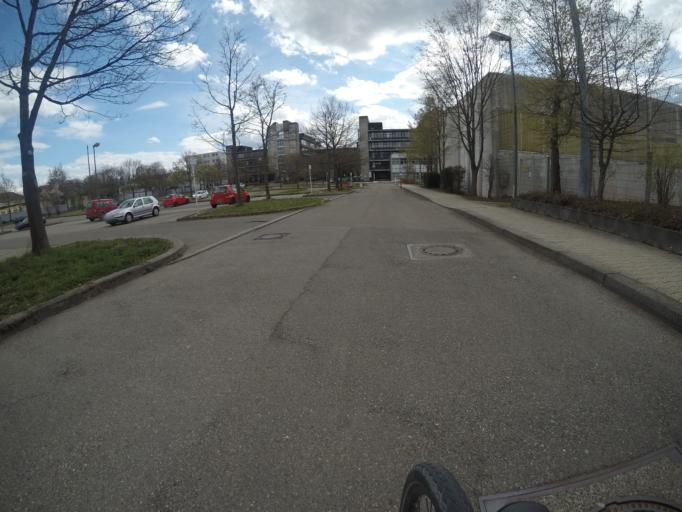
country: DE
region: Baden-Wuerttemberg
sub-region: Regierungsbezirk Stuttgart
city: Gerlingen
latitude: 48.7483
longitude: 9.1064
